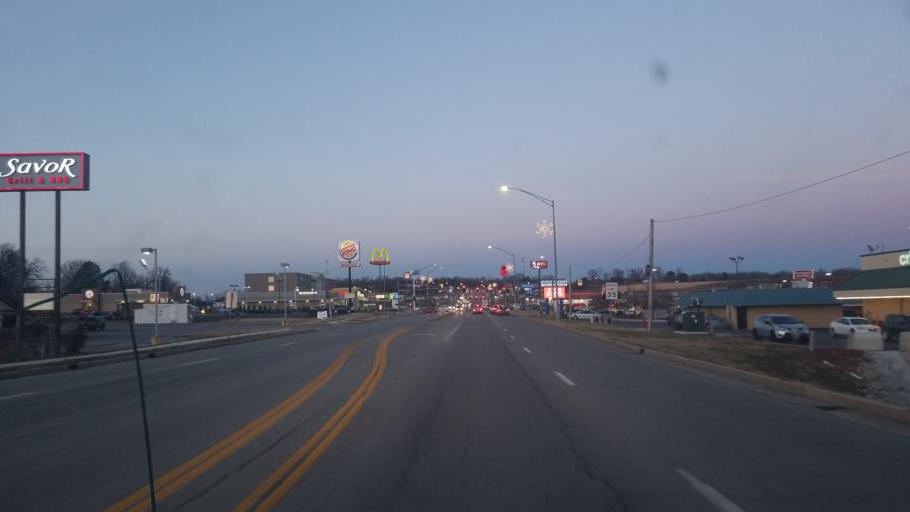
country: US
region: Missouri
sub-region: Howell County
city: West Plains
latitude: 36.7127
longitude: -91.8751
